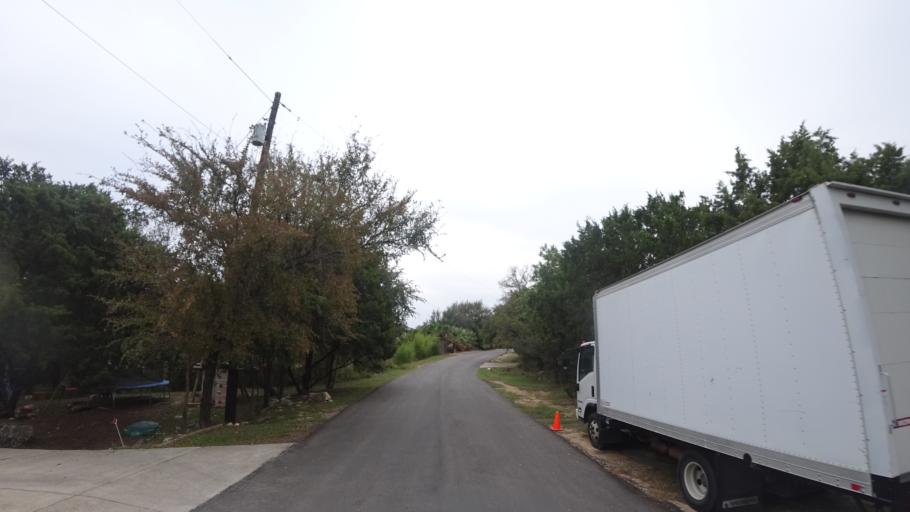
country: US
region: Texas
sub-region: Travis County
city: Hudson Bend
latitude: 30.3732
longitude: -97.9230
